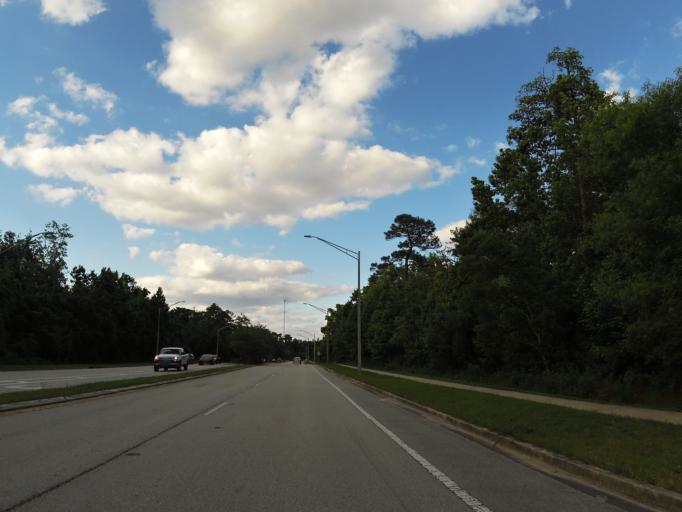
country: US
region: Florida
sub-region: Duval County
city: Jacksonville
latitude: 30.2557
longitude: -81.5631
